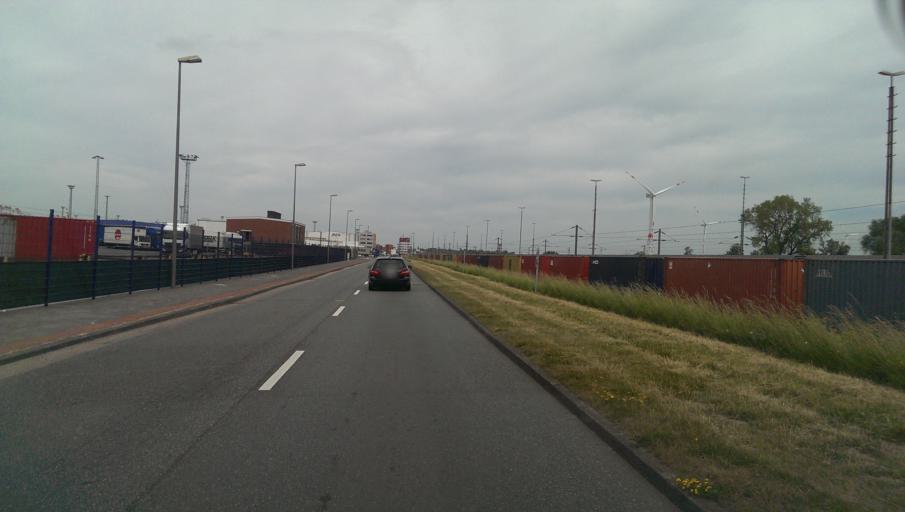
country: DE
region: Bremen
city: Bremerhaven
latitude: 53.5860
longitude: 8.5441
